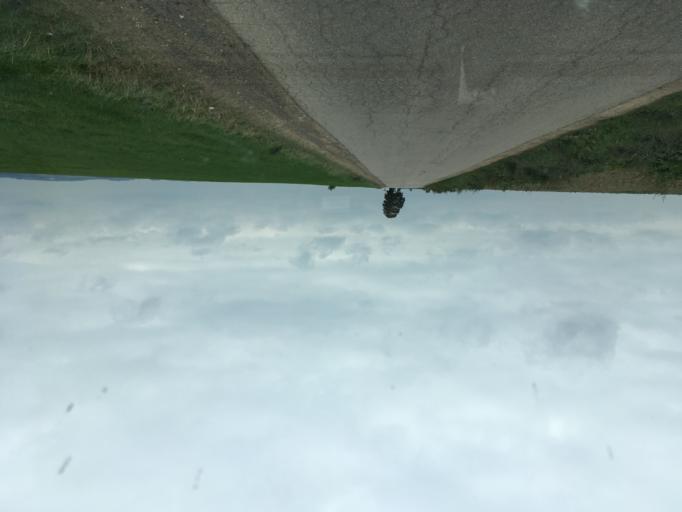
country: CZ
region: Central Bohemia
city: Vlasim
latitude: 49.7234
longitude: 14.8862
